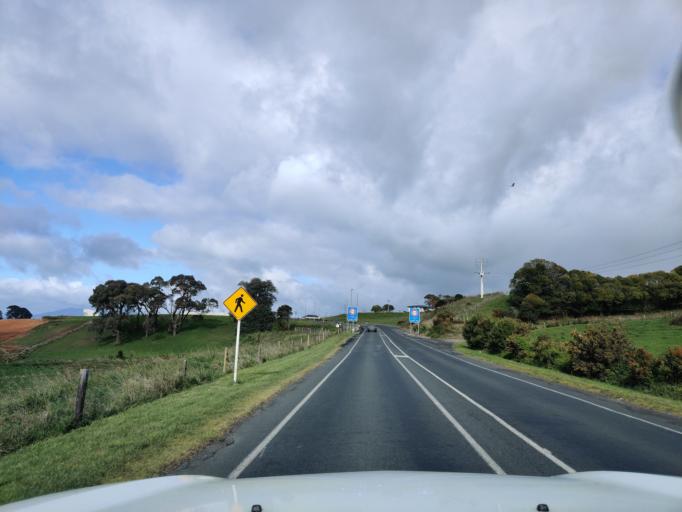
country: NZ
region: Waikato
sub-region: Hamilton City
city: Hamilton
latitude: -37.8164
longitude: 175.2287
